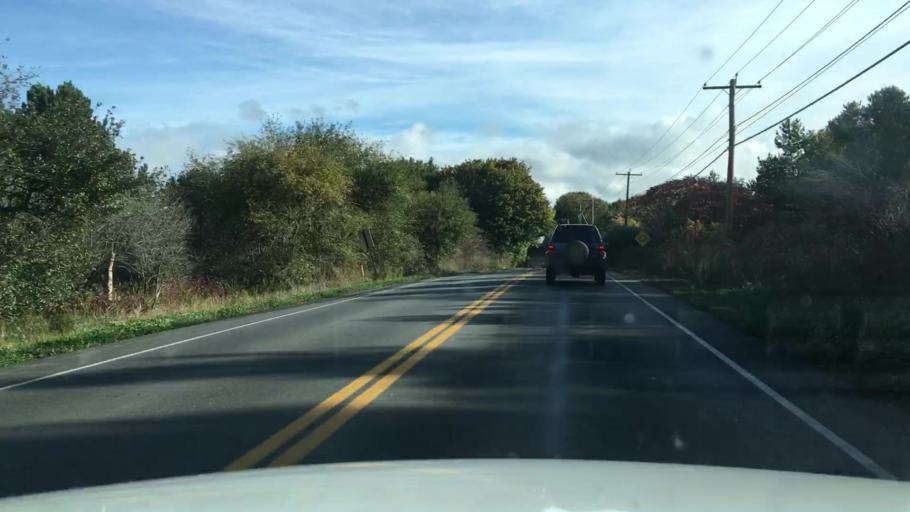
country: US
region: Maine
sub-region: Knox County
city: Rockland
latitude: 44.0999
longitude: -69.1459
